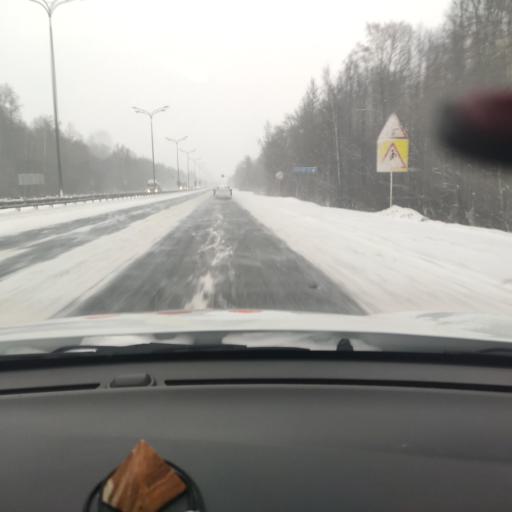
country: RU
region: Tatarstan
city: Sviyazhsk
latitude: 55.7434
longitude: 48.7915
